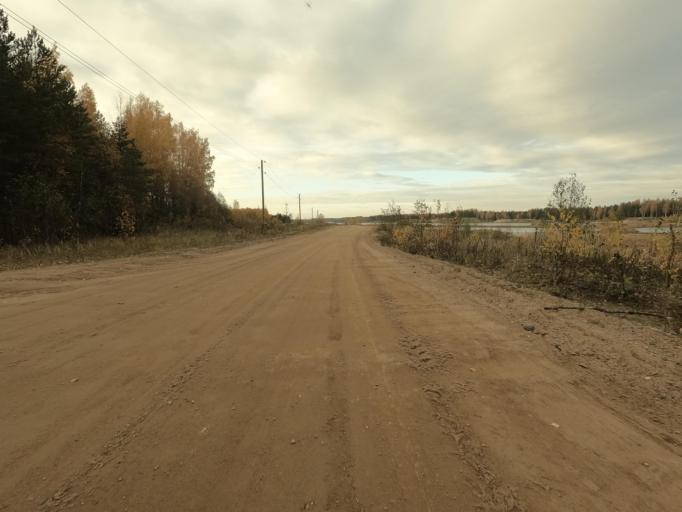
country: RU
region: Leningrad
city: Priladozhskiy
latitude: 59.7097
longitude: 31.3623
